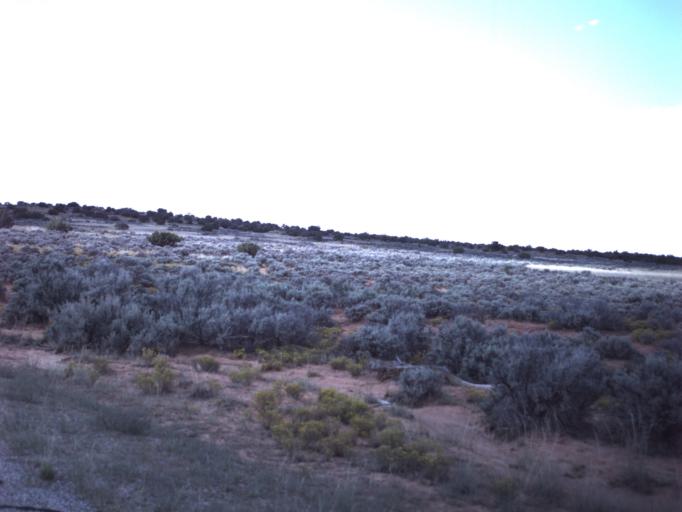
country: US
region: Utah
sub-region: Grand County
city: Moab
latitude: 38.5215
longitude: -109.7330
